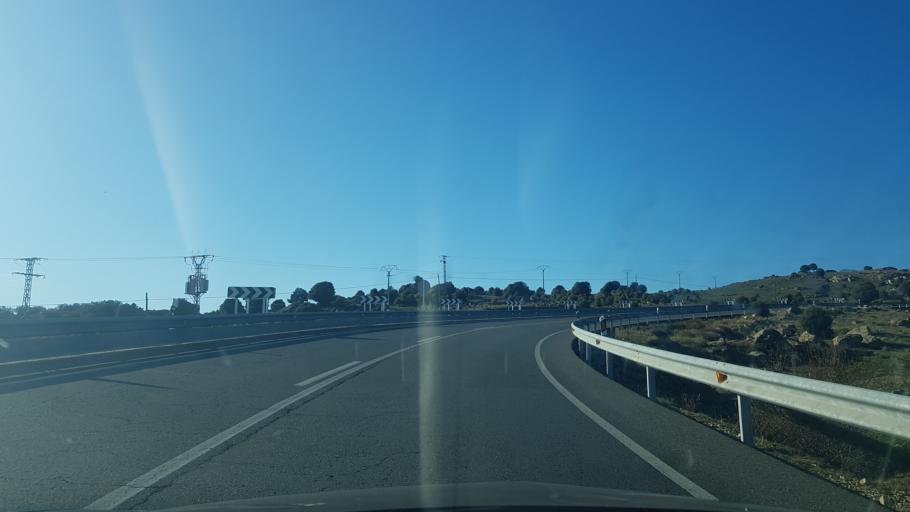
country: ES
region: Castille and Leon
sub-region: Provincia de Avila
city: Barraco
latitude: 40.4692
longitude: -4.6289
